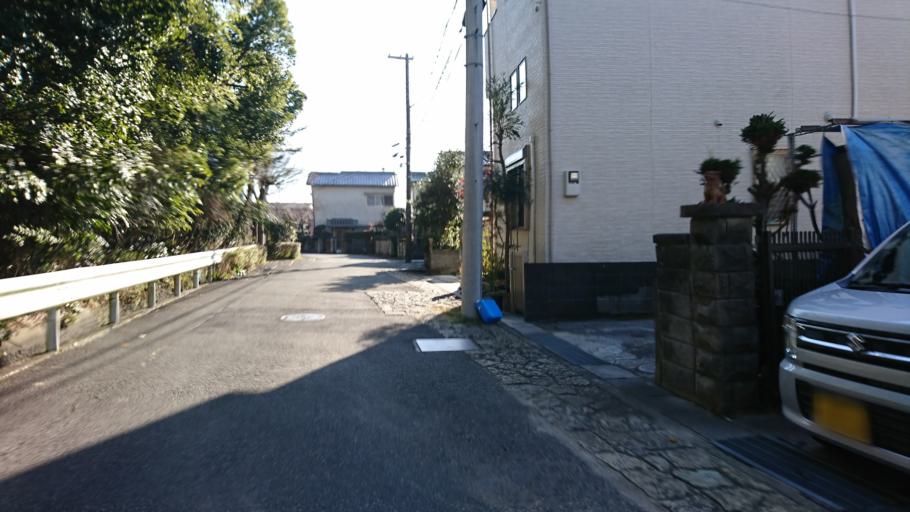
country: JP
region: Hyogo
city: Kakogawacho-honmachi
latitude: 34.7757
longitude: 134.8593
